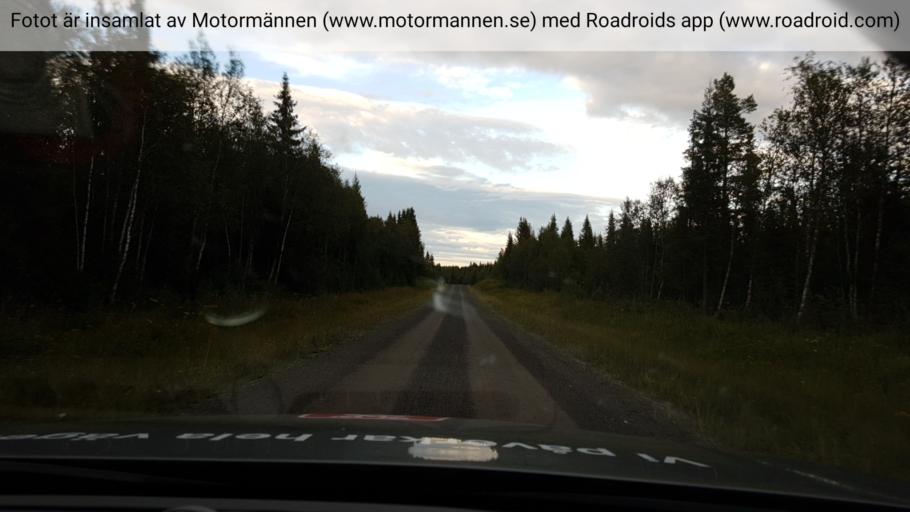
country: SE
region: Jaemtland
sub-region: OEstersunds Kommun
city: Lit
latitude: 63.4953
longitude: 15.2080
